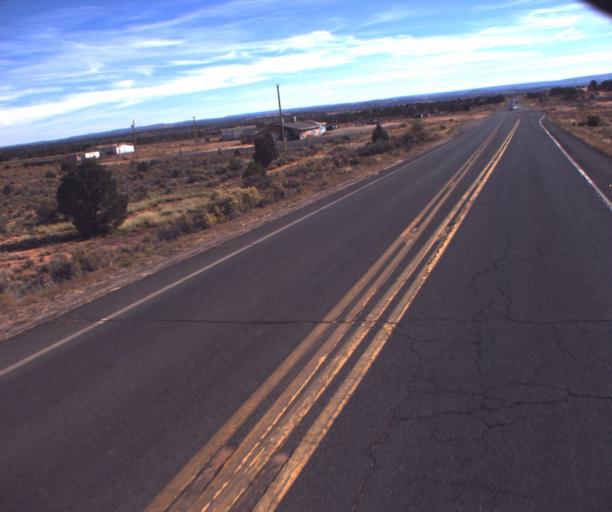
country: US
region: Arizona
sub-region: Coconino County
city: Kaibito
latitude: 36.5812
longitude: -110.7981
